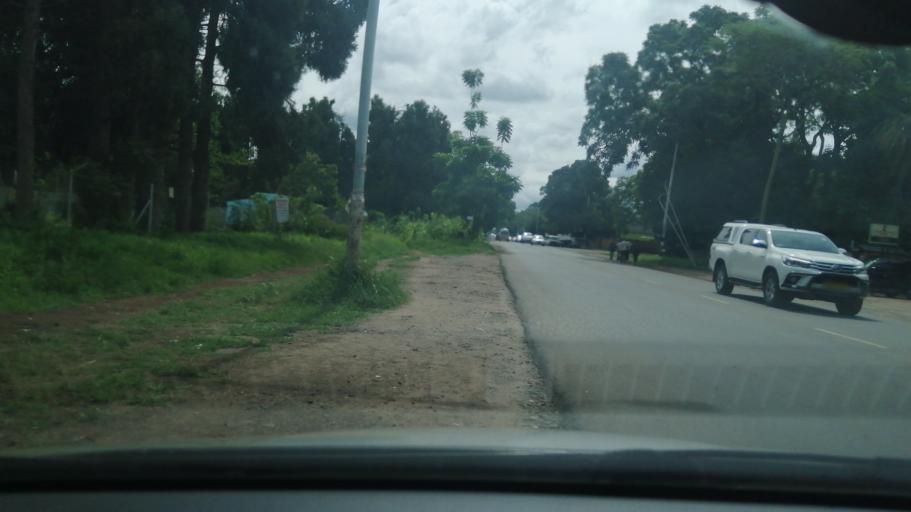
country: ZW
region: Harare
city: Harare
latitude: -17.8186
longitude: 31.0619
